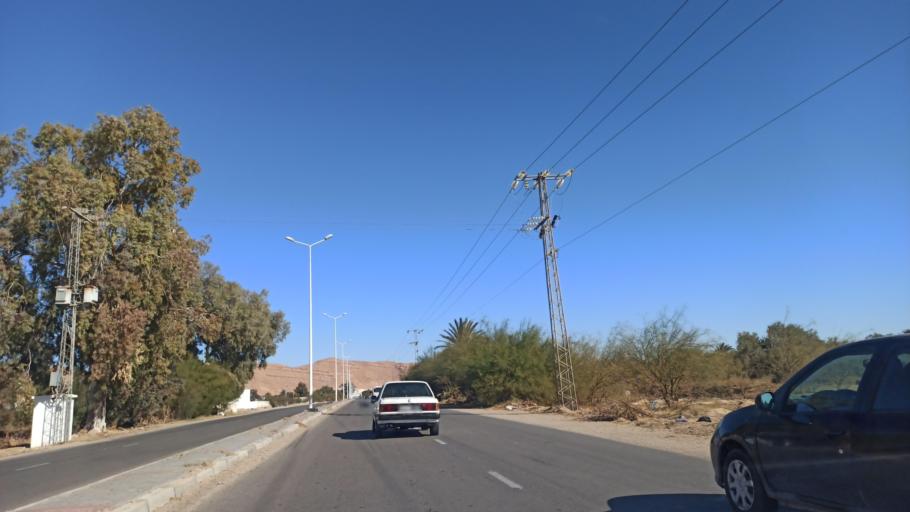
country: TN
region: Gafsa
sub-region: Gafsa Municipality
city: Gafsa
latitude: 34.4141
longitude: 8.7402
